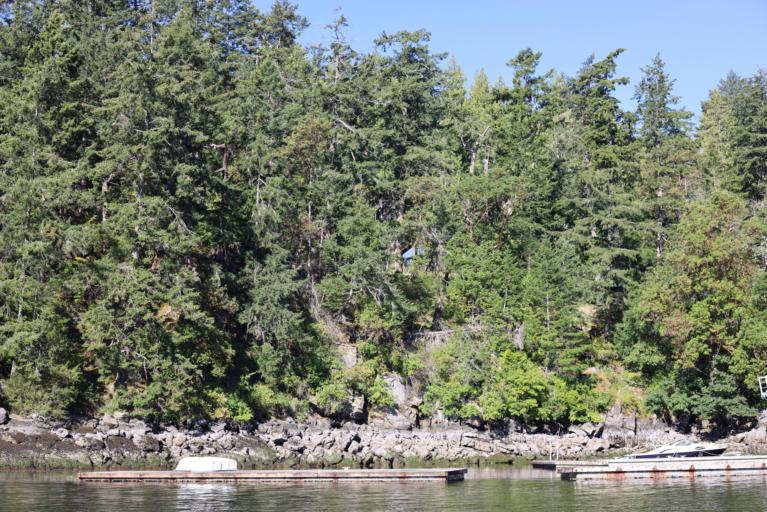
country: CA
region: British Columbia
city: North Cowichan
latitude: 48.7987
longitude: -123.5620
